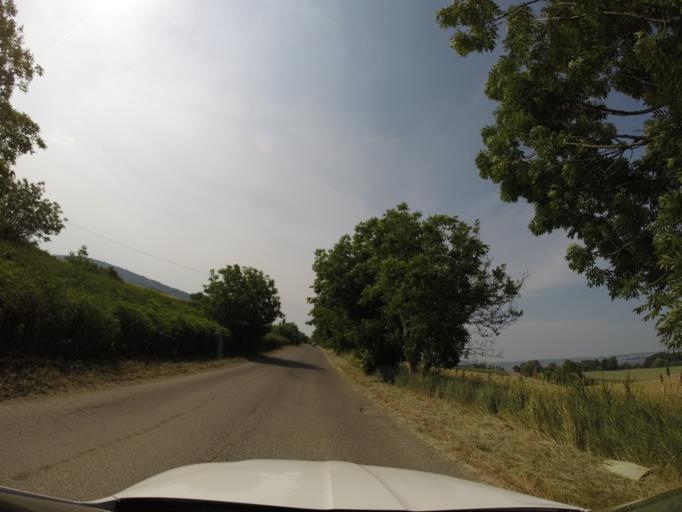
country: CZ
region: South Moravian
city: Sakvice
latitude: 48.8682
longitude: 16.6846
